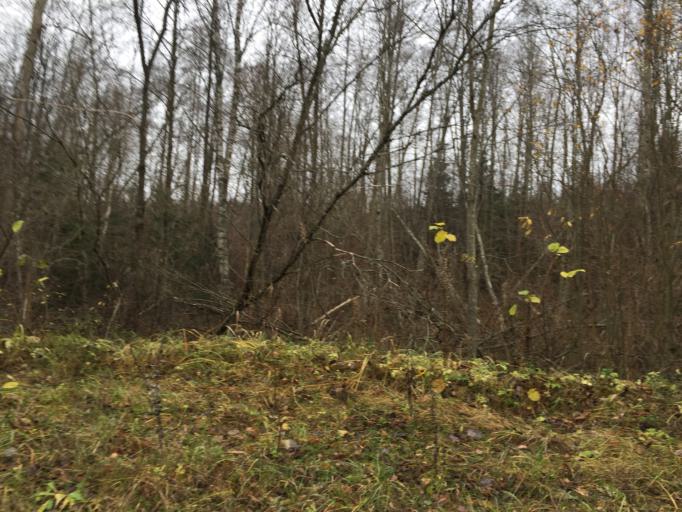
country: LV
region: Limbazu Rajons
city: Limbazi
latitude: 57.4206
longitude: 24.6315
